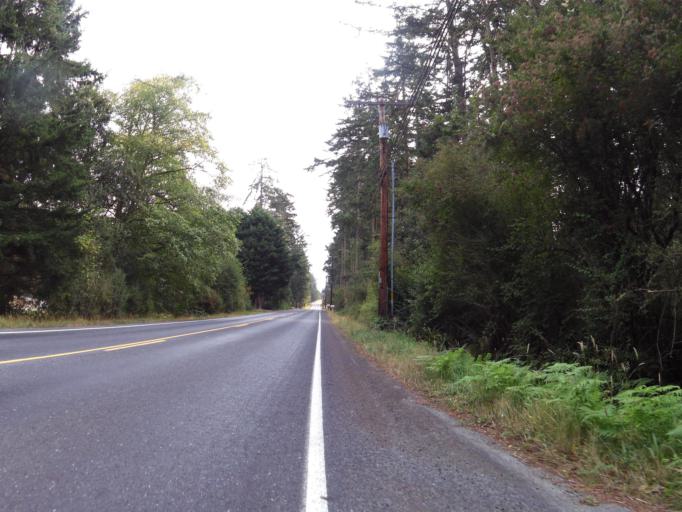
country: US
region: Washington
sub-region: Island County
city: Coupeville
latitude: 48.2319
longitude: -122.7474
